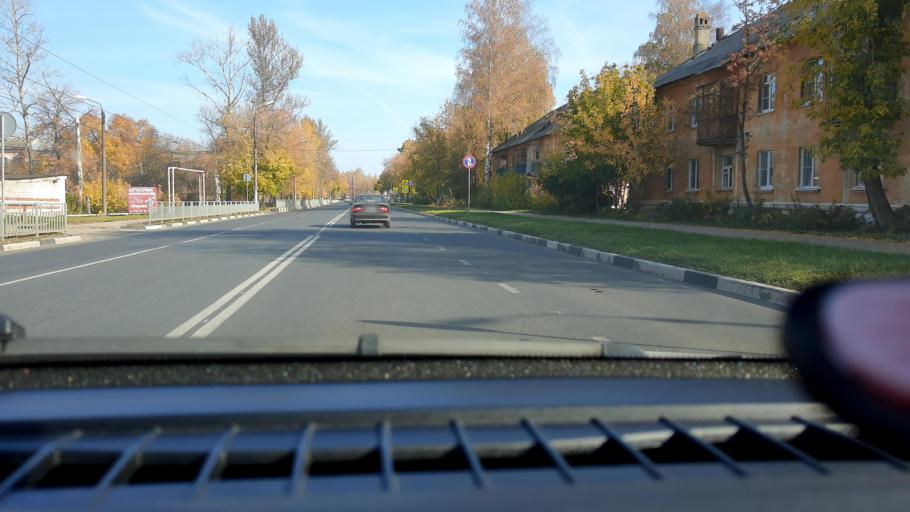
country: RU
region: Nizjnij Novgorod
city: Kstovo
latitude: 56.1543
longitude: 44.1933
